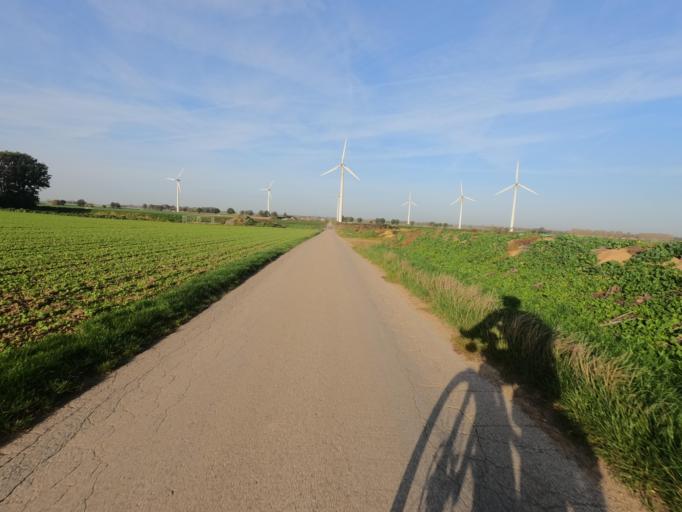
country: DE
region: North Rhine-Westphalia
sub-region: Regierungsbezirk Koln
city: Titz
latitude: 51.0624
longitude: 6.4172
